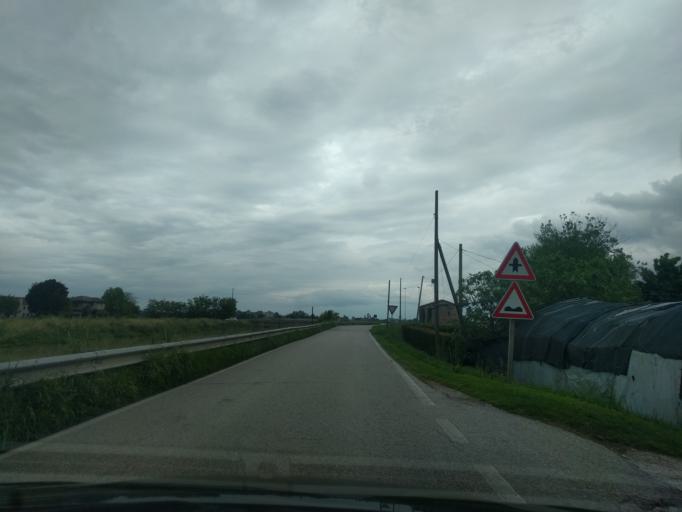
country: IT
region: Veneto
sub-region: Provincia di Rovigo
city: Mardimago
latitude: 45.0947
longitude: 11.8450
